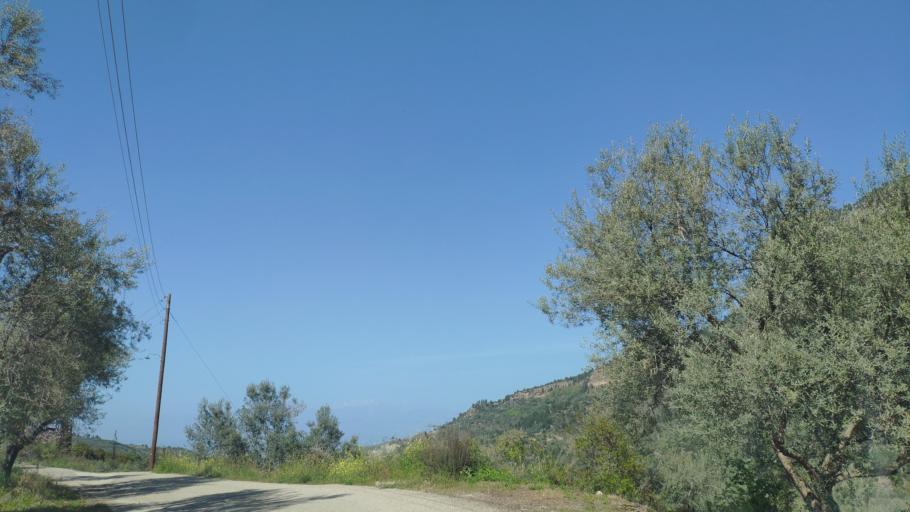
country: GR
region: West Greece
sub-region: Nomos Achaias
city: Aiyira
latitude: 38.0821
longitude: 22.3376
